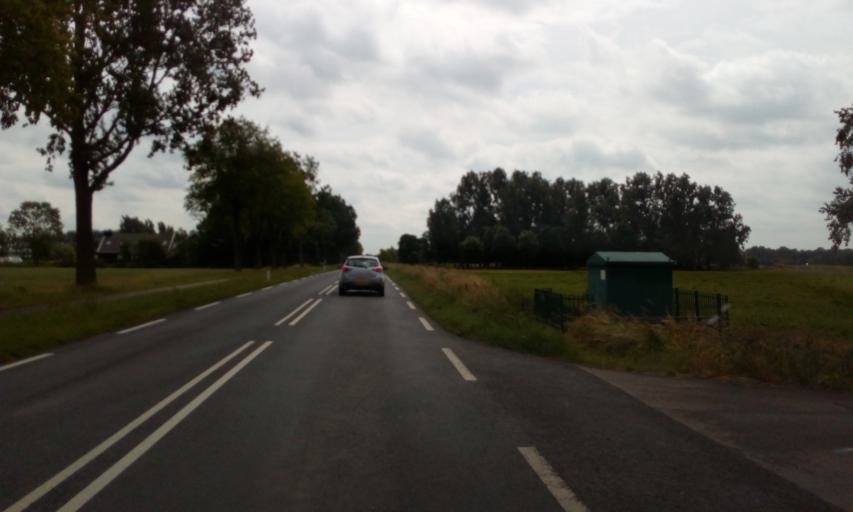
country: NL
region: South Holland
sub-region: Gemeente Waddinxveen
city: Waddinxveen
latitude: 52.0043
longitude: 4.6417
